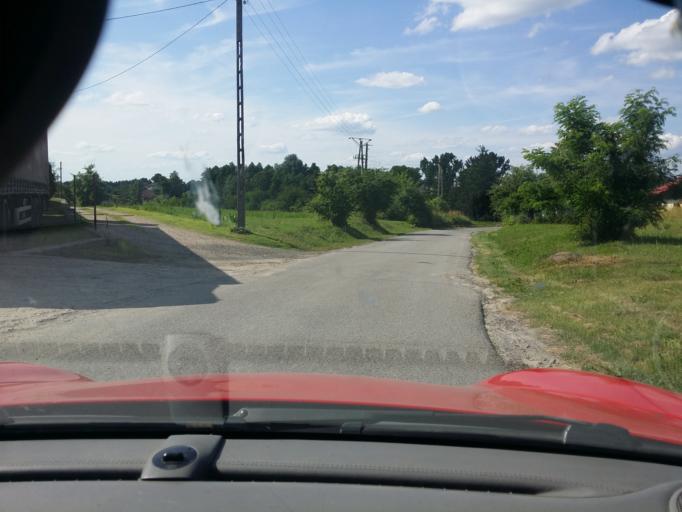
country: PL
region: Masovian Voivodeship
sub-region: Powiat radomski
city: Trablice
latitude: 51.3483
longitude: 21.1368
